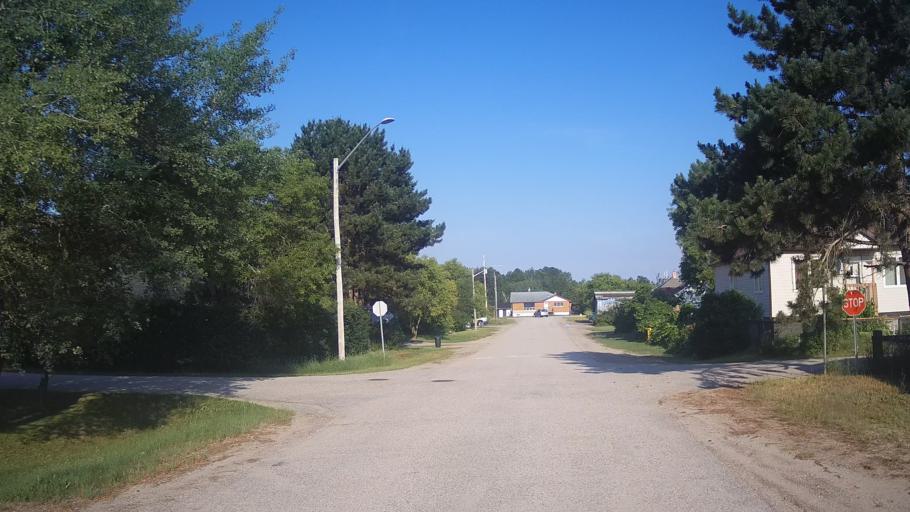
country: CA
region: Ontario
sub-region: Rainy River District
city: Atikokan
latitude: 49.4176
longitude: -91.6623
